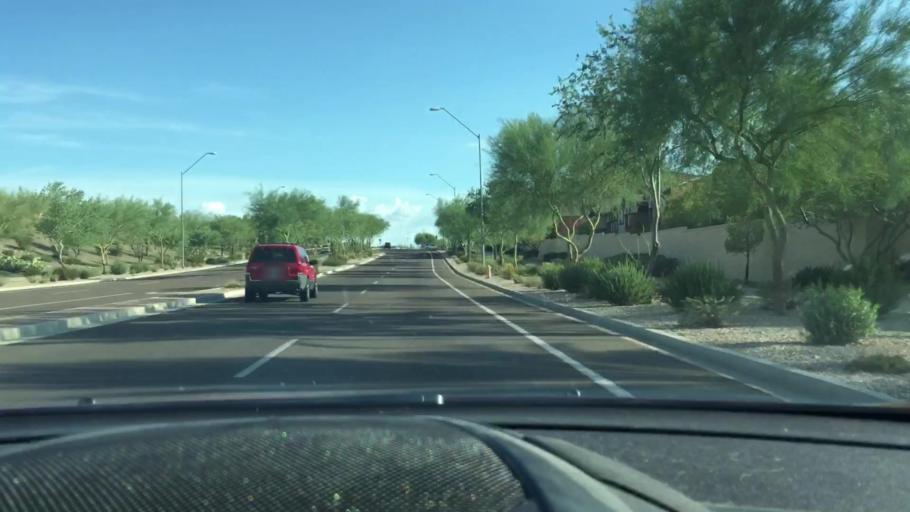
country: US
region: Arizona
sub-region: Maricopa County
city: Sun City West
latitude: 33.7166
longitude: -112.2853
